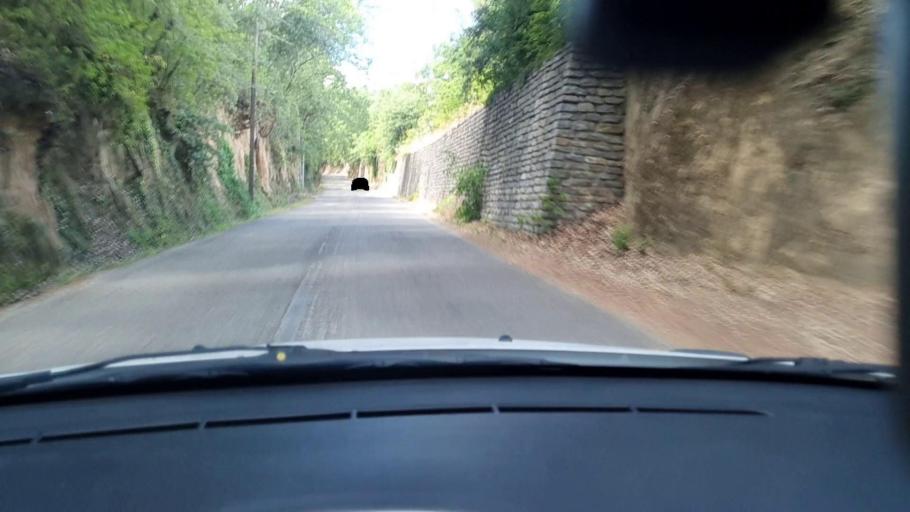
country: FR
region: Languedoc-Roussillon
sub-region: Departement du Gard
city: Cabrieres
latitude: 43.9544
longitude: 4.4739
